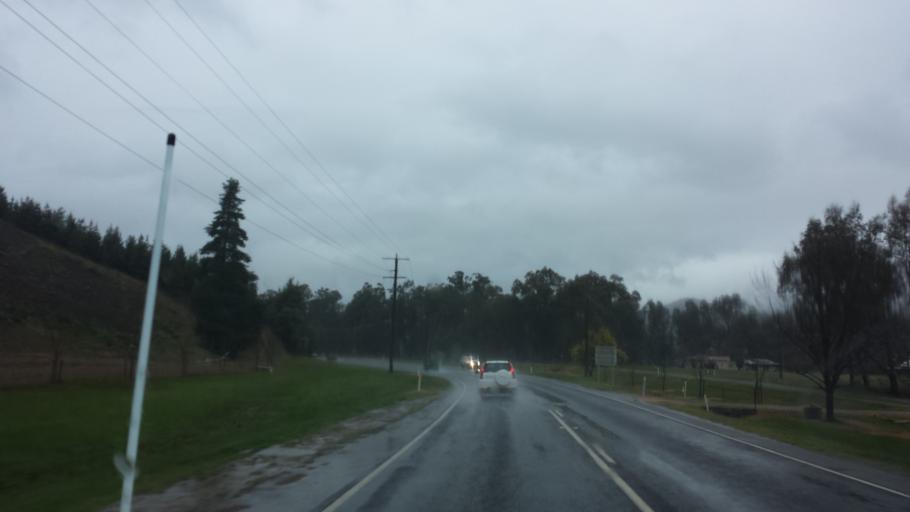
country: AU
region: Victoria
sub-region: Alpine
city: Mount Beauty
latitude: -36.5799
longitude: 146.7503
